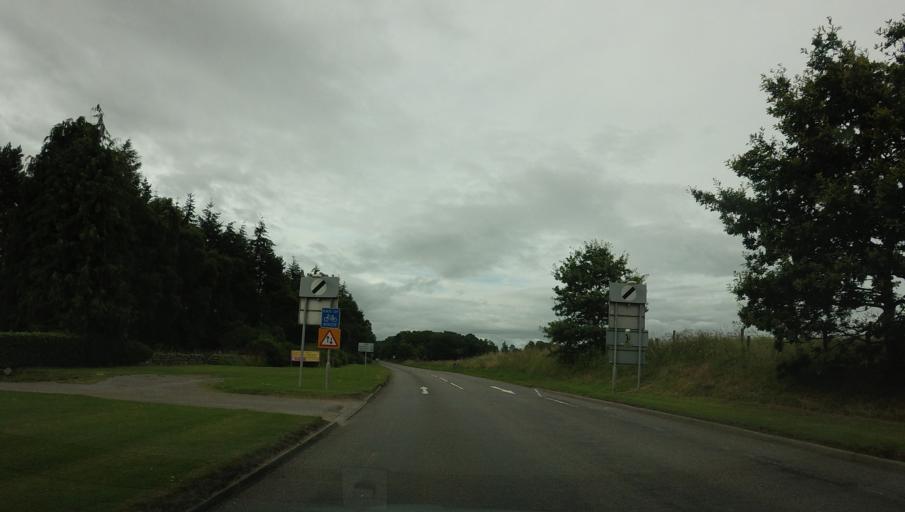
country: GB
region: Scotland
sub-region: Aberdeenshire
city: Aboyne
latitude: 57.0790
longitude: -2.7668
